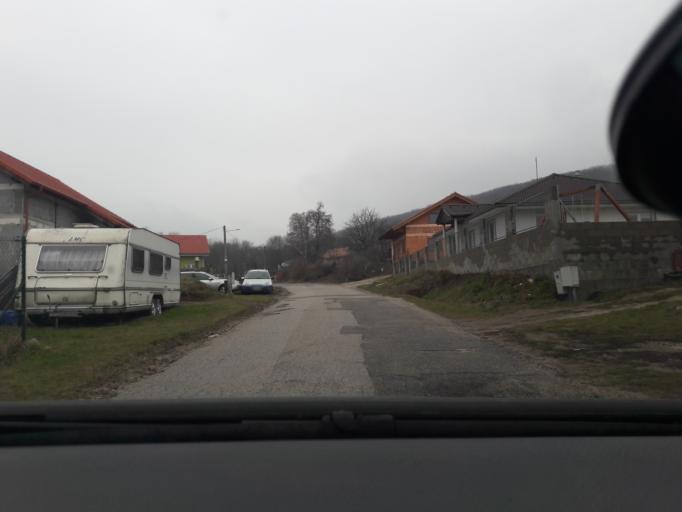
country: SK
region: Trnavsky
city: Smolenice
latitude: 48.4923
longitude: 17.4133
